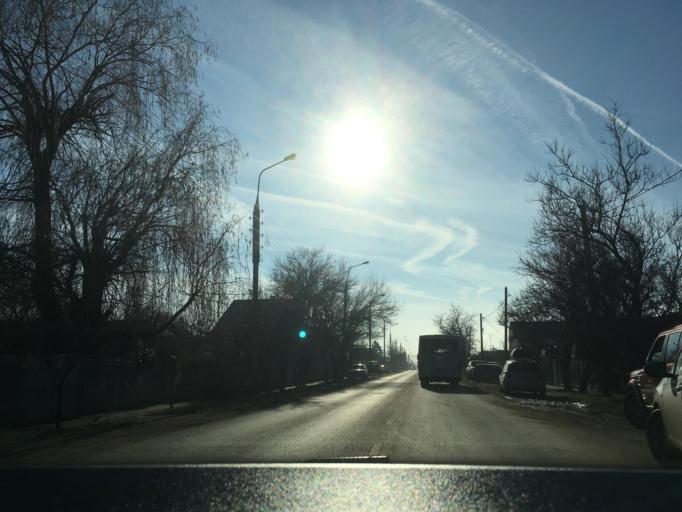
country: RU
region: Krasnodarskiy
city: Krasnodar
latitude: 45.1224
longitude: 39.0113
